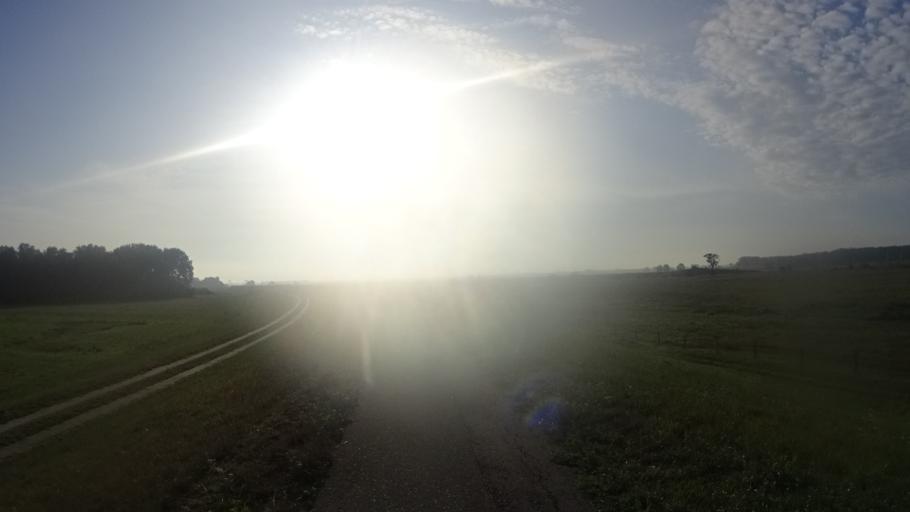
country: DE
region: Brandenburg
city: Lenzen
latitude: 53.0565
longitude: 11.5325
